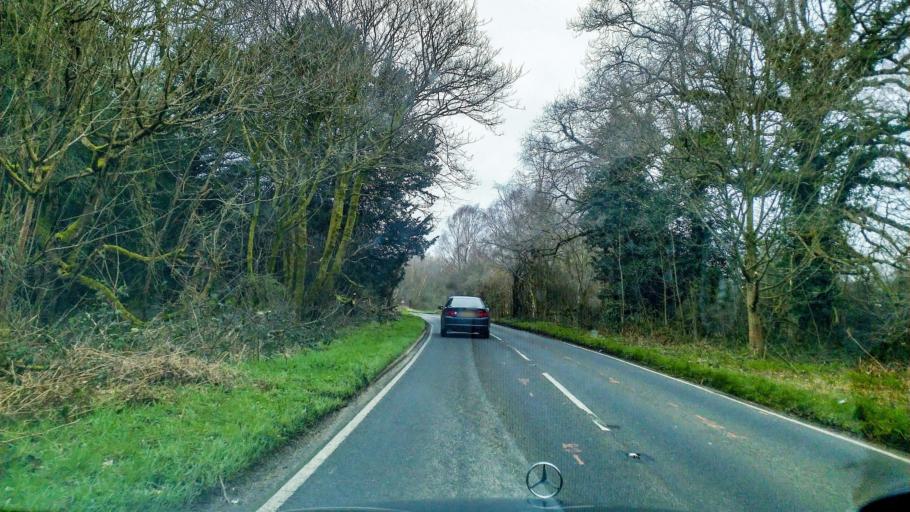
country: GB
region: England
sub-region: Surrey
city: Chilworth
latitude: 51.2365
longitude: -0.5104
